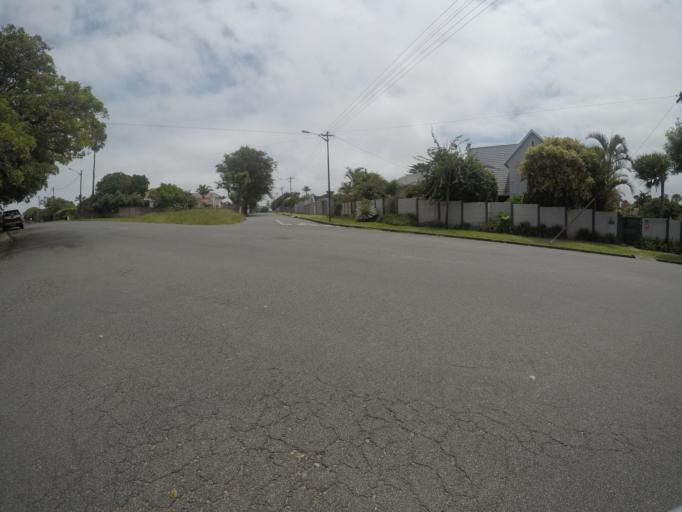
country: ZA
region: Eastern Cape
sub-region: Buffalo City Metropolitan Municipality
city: East London
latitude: -32.9918
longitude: 27.9290
